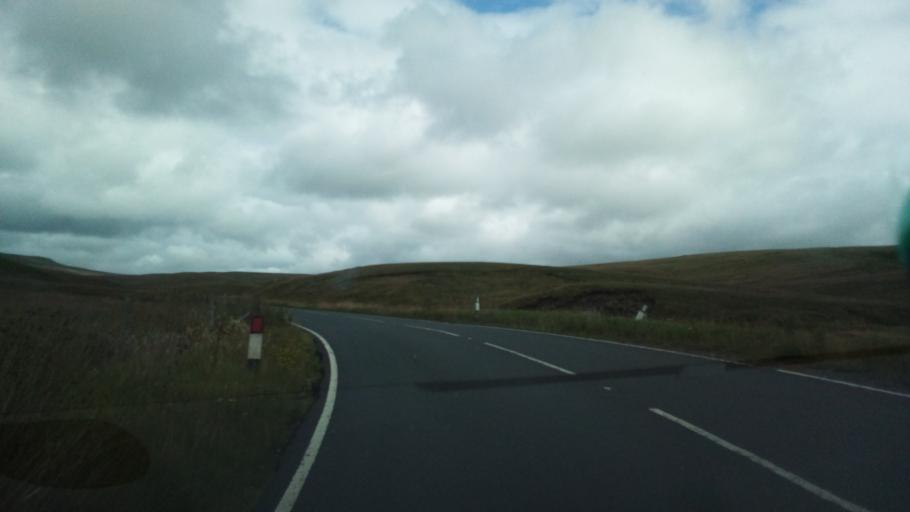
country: GB
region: England
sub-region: North Yorkshire
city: Settle
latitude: 54.2295
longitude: -2.3196
